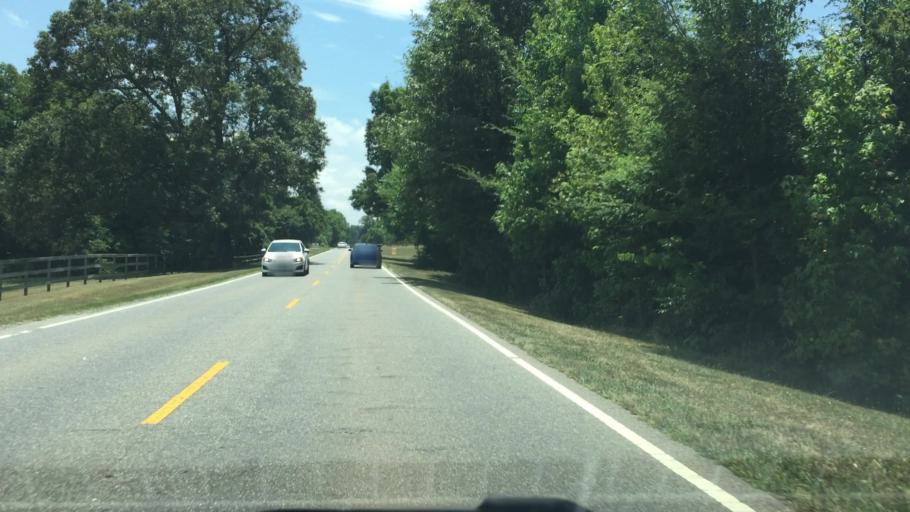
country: US
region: North Carolina
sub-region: Iredell County
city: Mooresville
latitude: 35.5271
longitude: -80.7695
